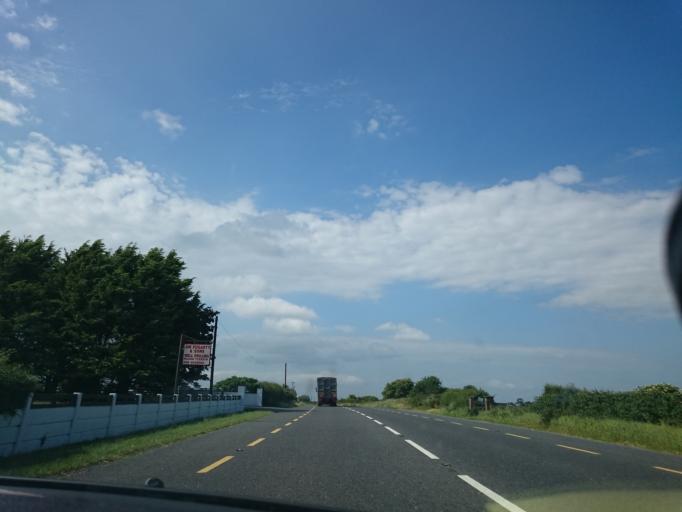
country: IE
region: Leinster
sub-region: Kilkenny
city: Kilkenny
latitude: 52.6071
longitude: -7.2431
